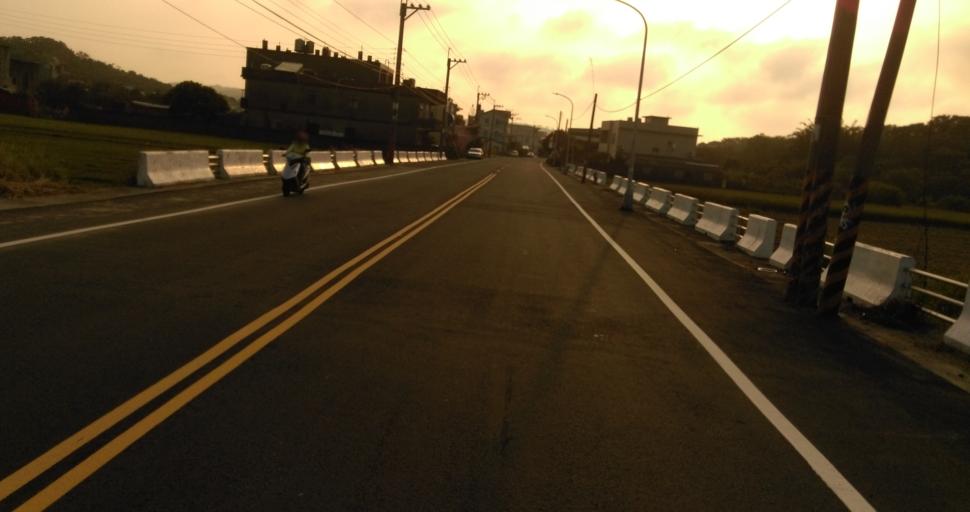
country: TW
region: Taiwan
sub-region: Hsinchu
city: Hsinchu
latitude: 24.7450
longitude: 120.9177
